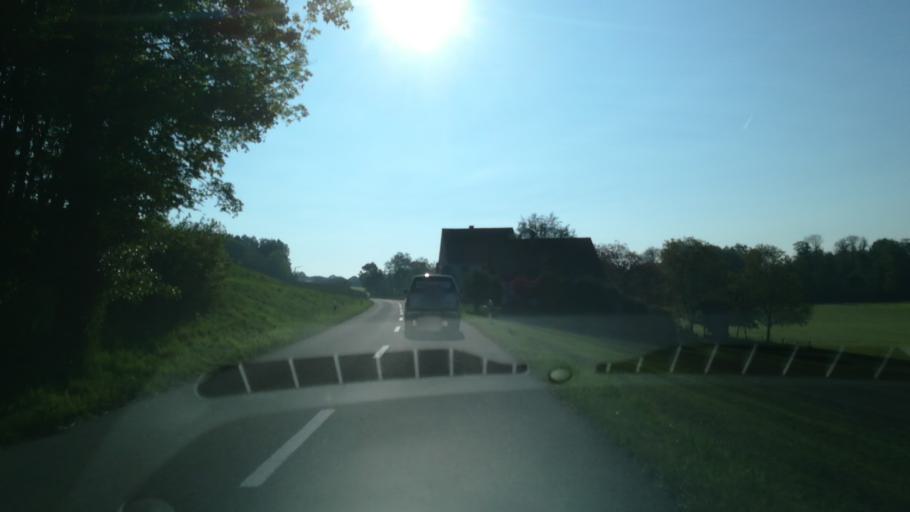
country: CH
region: Thurgau
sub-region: Frauenfeld District
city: Homburg
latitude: 47.6346
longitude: 9.0136
